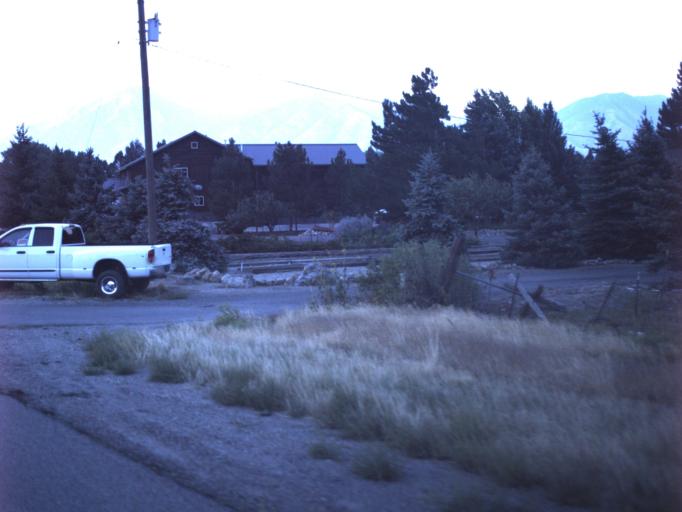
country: US
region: Utah
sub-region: Utah County
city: Mapleton
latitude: 40.1026
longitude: -111.5971
